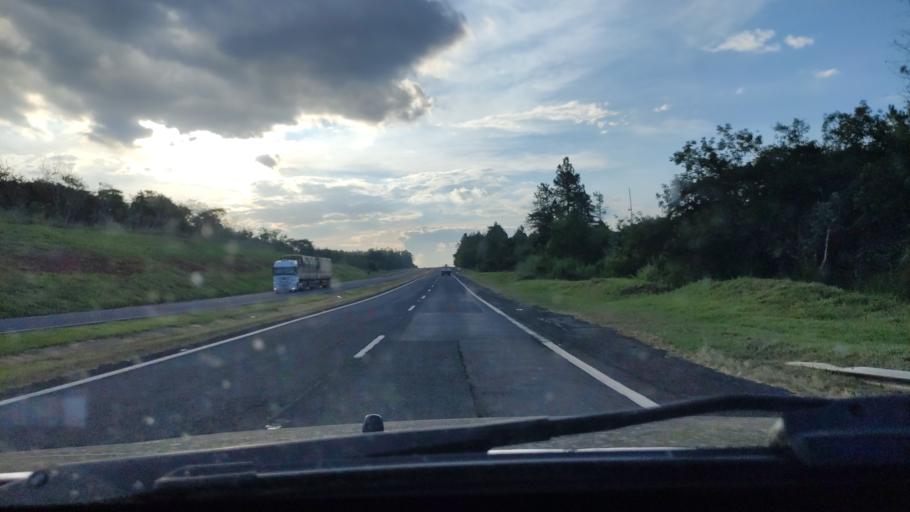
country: BR
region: Sao Paulo
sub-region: Rancharia
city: Rancharia
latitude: -22.4712
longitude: -50.9462
